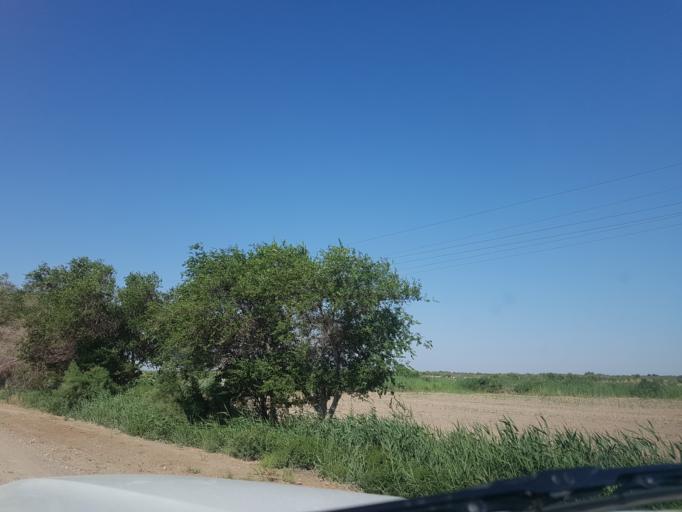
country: TM
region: Dasoguz
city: Koeneuergench
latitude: 42.1297
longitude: 58.9447
